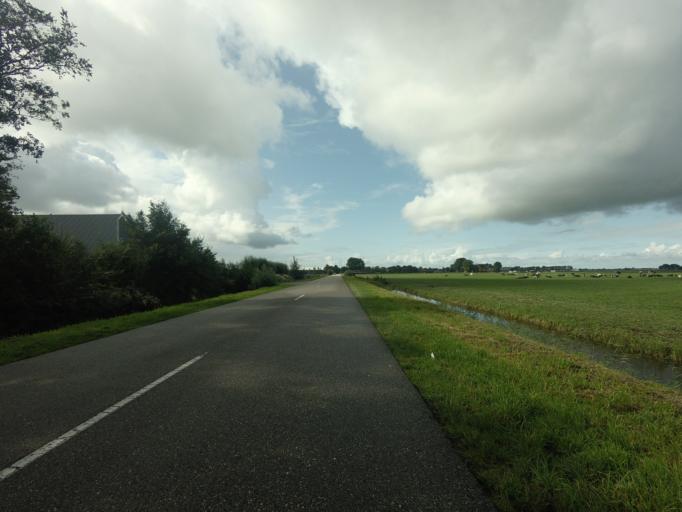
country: NL
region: Friesland
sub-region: Gemeente Boarnsterhim
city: Warten
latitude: 53.1544
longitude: 5.9104
